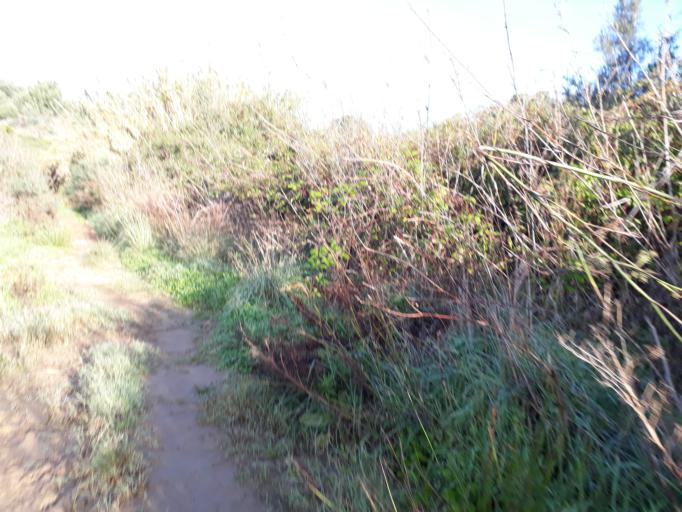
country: ES
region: Andalusia
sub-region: Provincia de Malaga
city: Fuengirola
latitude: 36.5041
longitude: -4.6985
